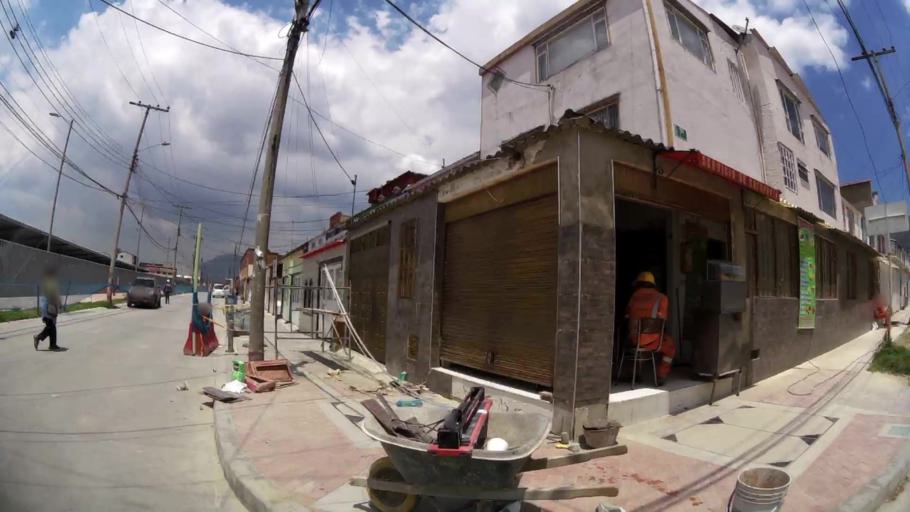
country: CO
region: Bogota D.C.
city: Bogota
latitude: 4.5757
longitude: -74.0937
